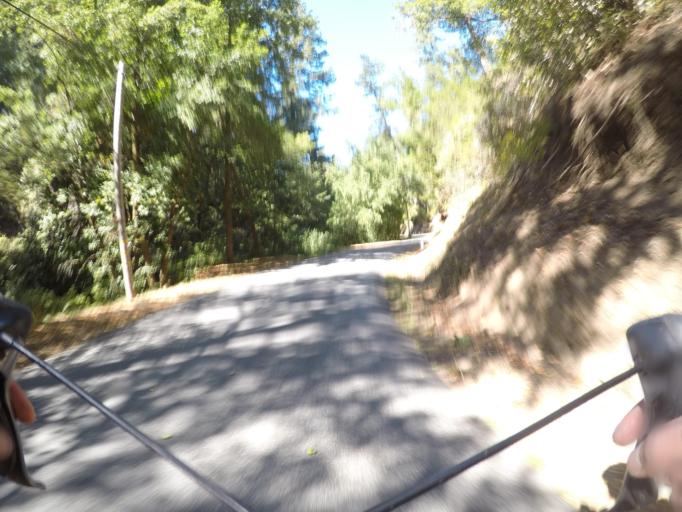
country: US
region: California
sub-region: San Mateo County
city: Portola Valley
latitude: 37.2951
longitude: -122.2442
